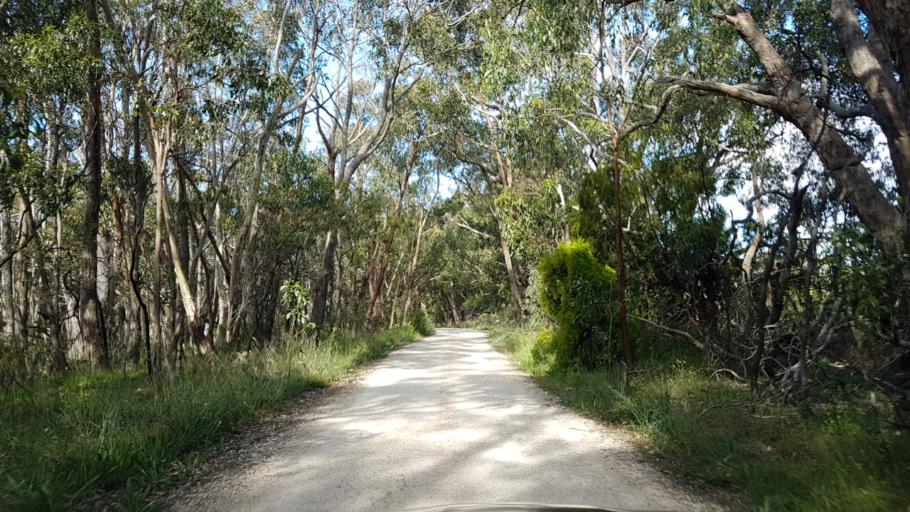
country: AU
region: South Australia
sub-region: Adelaide Hills
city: Adelaide Hills
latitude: -34.9066
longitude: 138.7381
